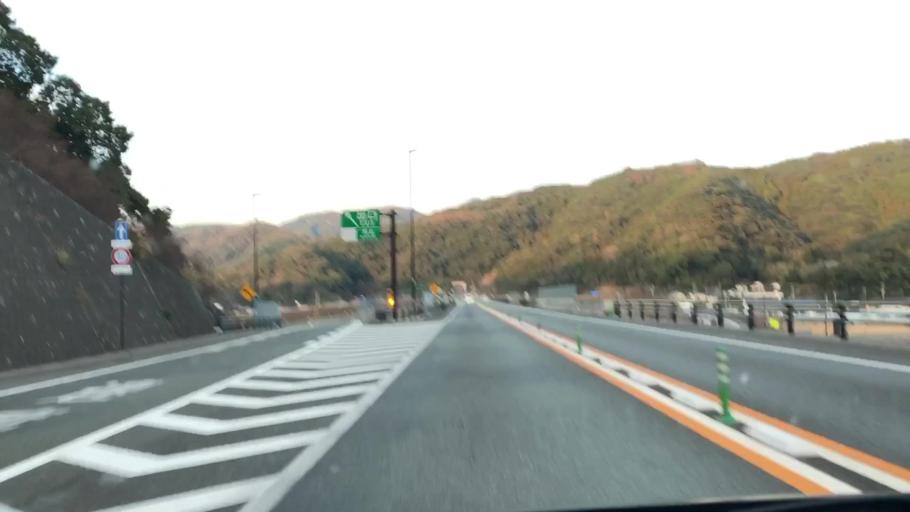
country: JP
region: Kumamoto
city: Minamata
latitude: 32.2965
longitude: 130.5084
